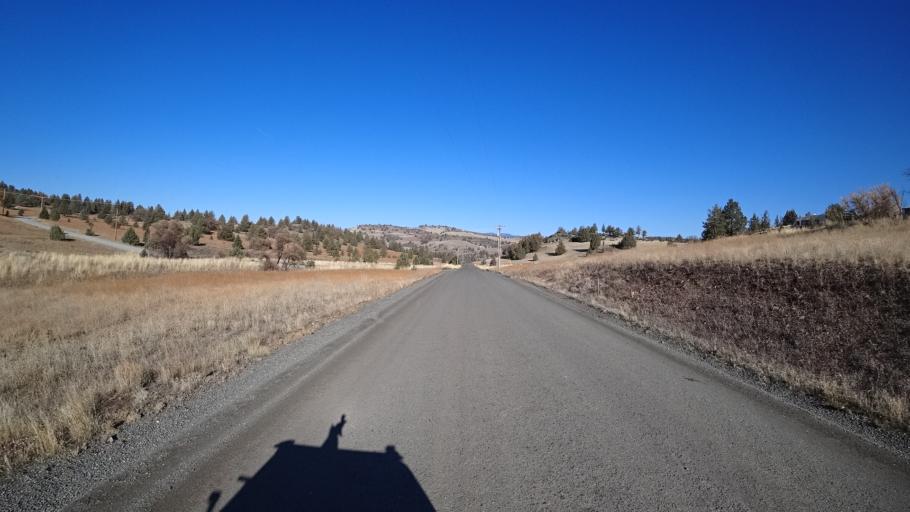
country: US
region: California
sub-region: Siskiyou County
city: Montague
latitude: 41.8828
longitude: -122.4253
